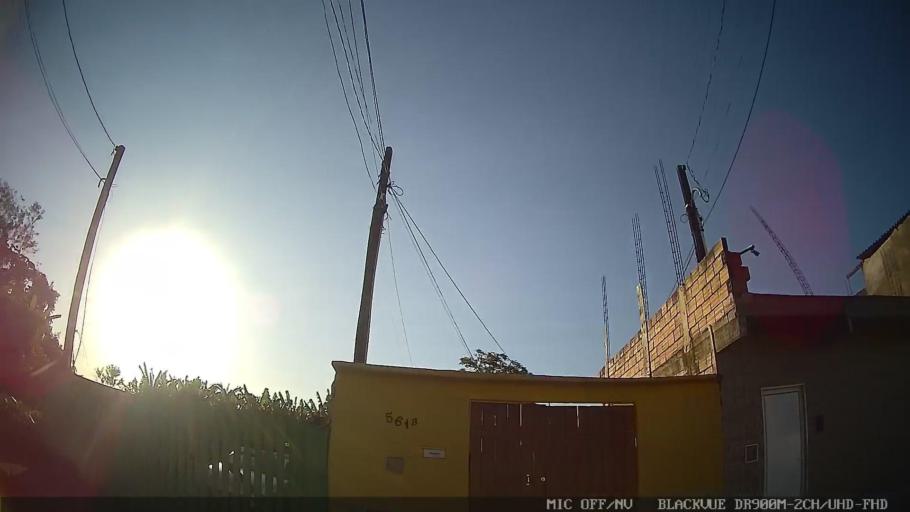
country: BR
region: Sao Paulo
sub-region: Guaruja
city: Guaruja
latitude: -23.9684
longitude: -46.2733
